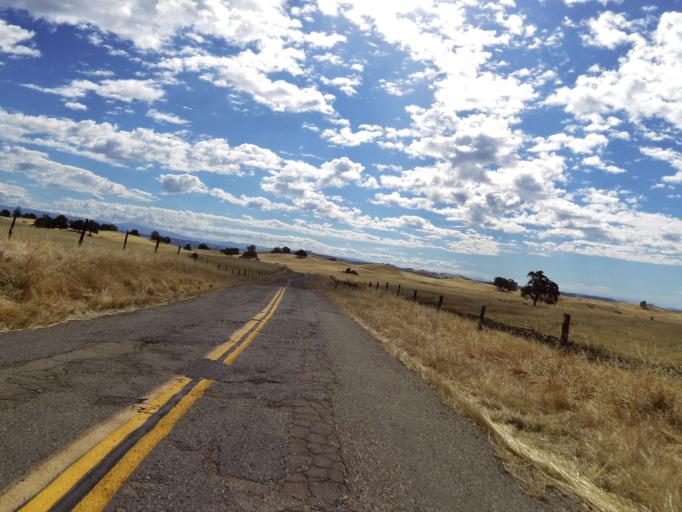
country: US
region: California
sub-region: Madera County
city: Bonadelle Ranchos-Madera Ranchos
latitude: 37.0418
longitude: -119.7653
